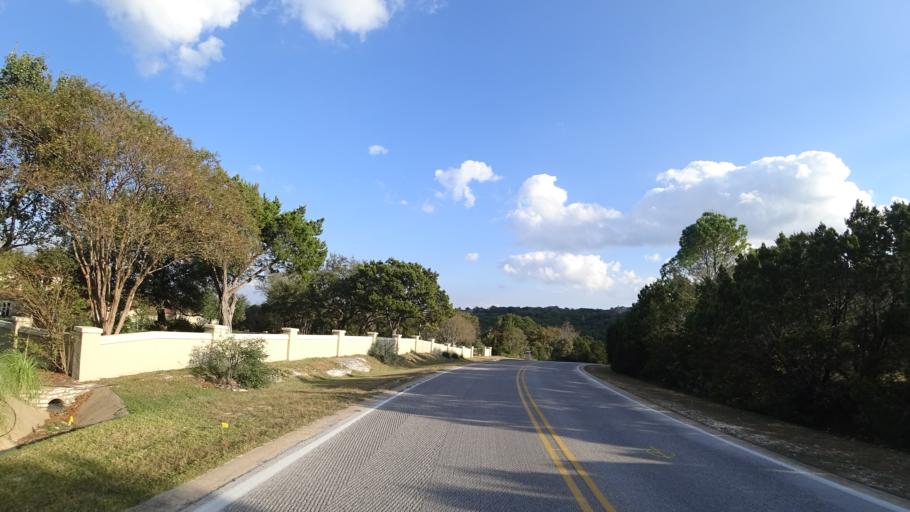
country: US
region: Texas
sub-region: Travis County
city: Barton Creek
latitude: 30.2780
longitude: -97.8694
